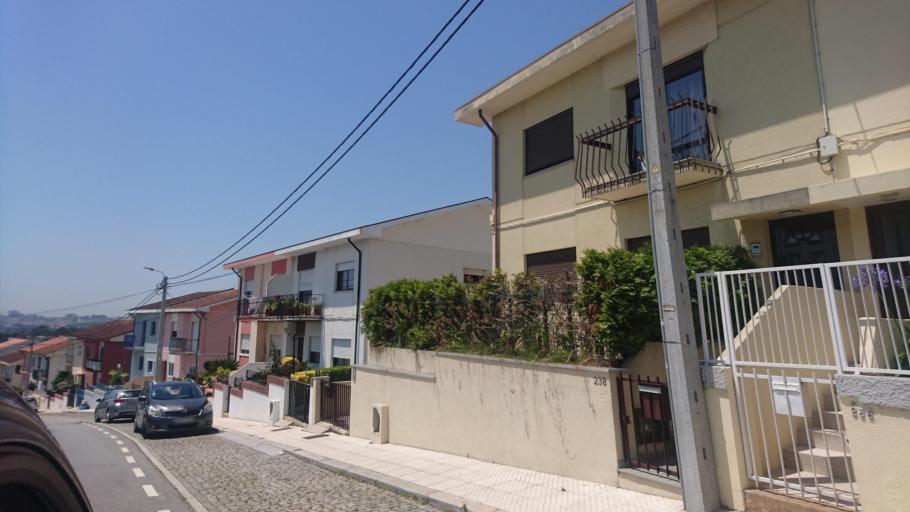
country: PT
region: Porto
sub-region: Gondomar
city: Rio Tinto
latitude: 41.1605
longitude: -8.5520
